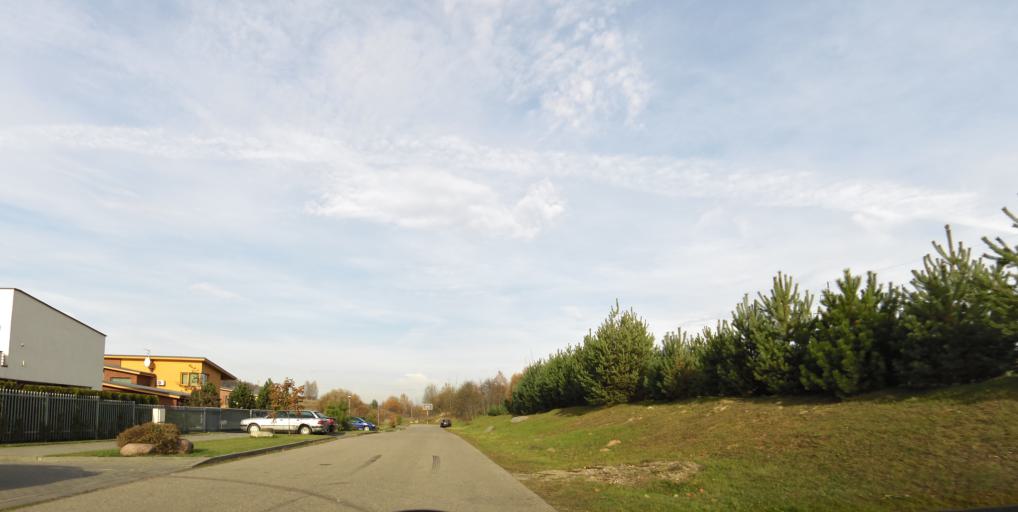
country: LT
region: Vilnius County
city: Justiniskes
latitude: 54.7134
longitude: 25.2061
